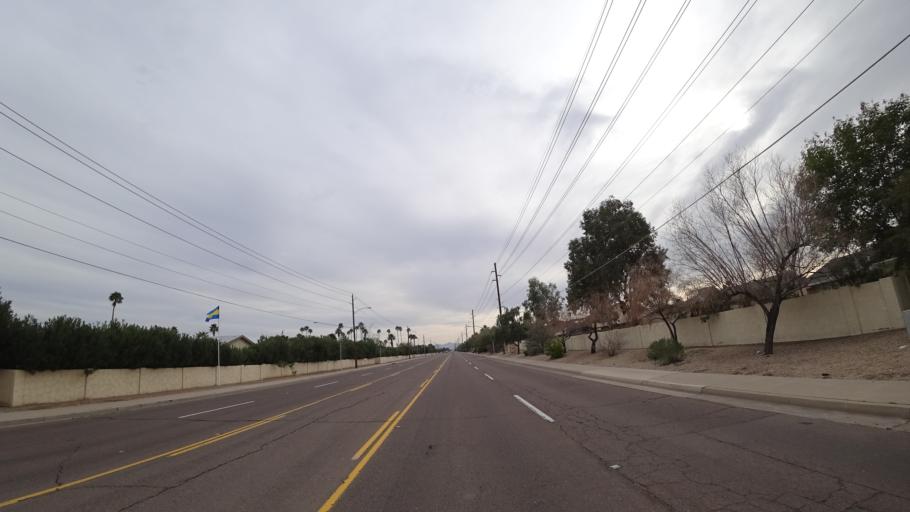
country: US
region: Arizona
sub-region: Maricopa County
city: Sun City
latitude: 33.5899
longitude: -112.2552
